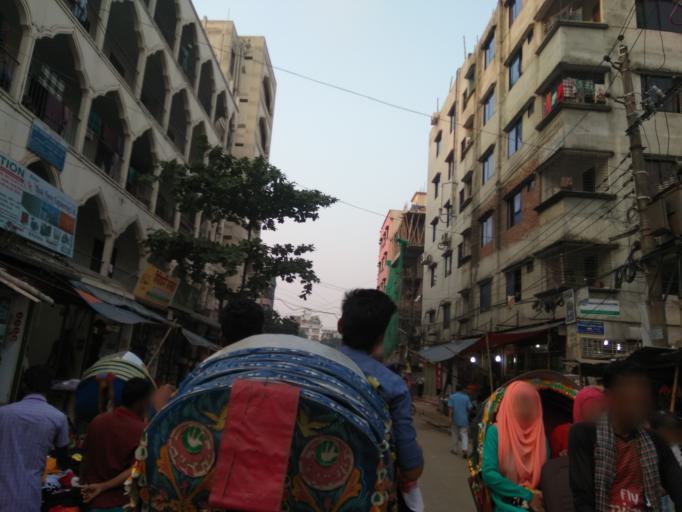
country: BD
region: Dhaka
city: Azimpur
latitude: 23.8103
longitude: 90.3642
